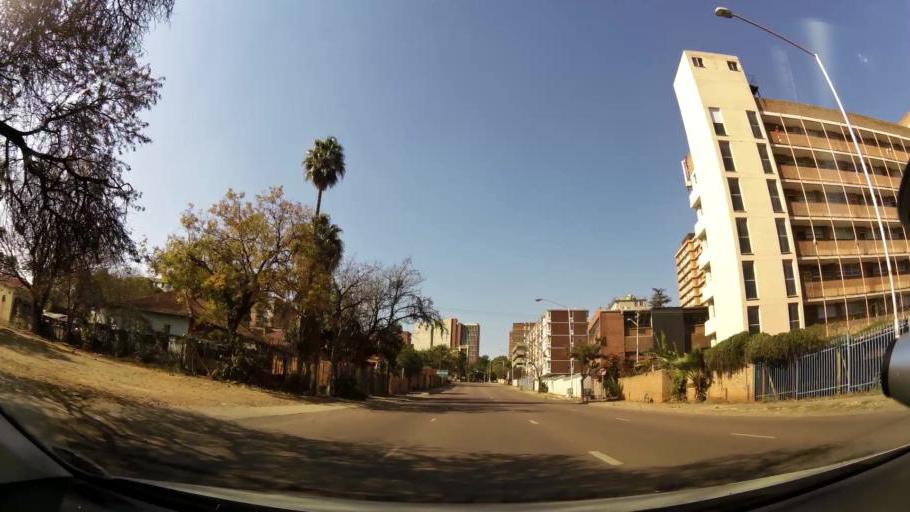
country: ZA
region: Gauteng
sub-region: City of Tshwane Metropolitan Municipality
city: Pretoria
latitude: -25.7413
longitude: 28.2012
